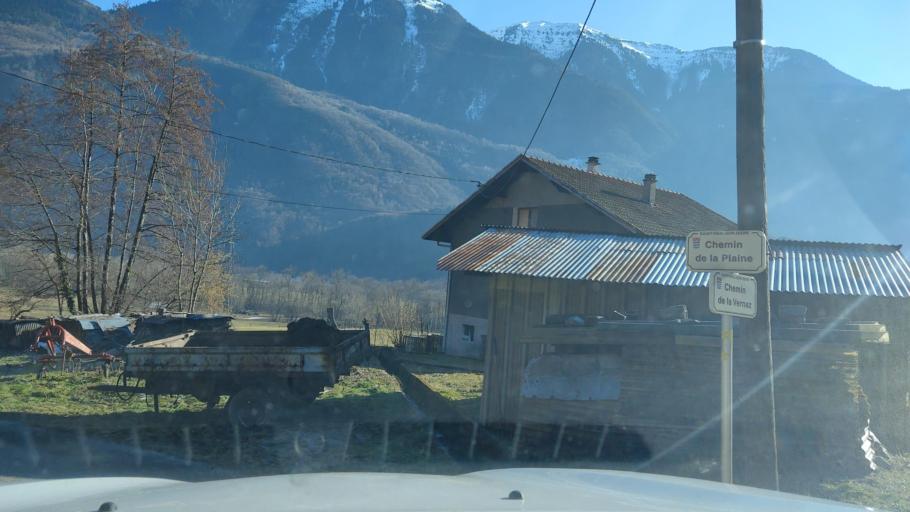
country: FR
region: Rhone-Alpes
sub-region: Departement de la Savoie
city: La Bathie
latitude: 45.5987
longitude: 6.4395
